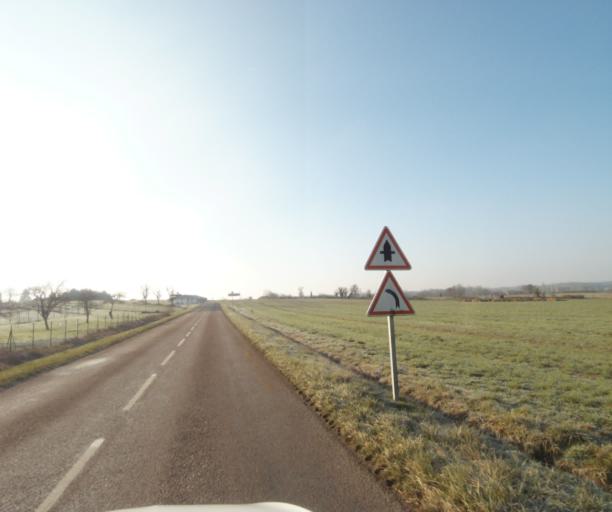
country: FR
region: Champagne-Ardenne
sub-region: Departement de la Haute-Marne
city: Montier-en-Der
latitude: 48.4161
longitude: 4.7422
